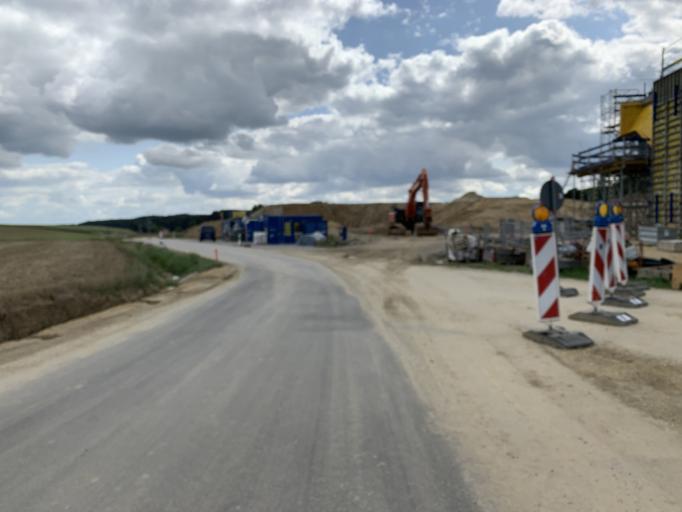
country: DE
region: Bavaria
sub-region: Upper Bavaria
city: Zolling
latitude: 48.4311
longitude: 11.7722
